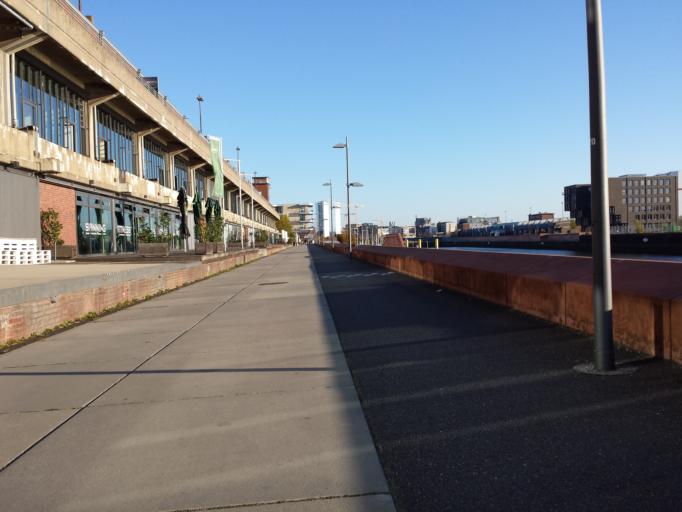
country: DE
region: Bremen
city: Bremen
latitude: 53.0902
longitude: 8.7741
